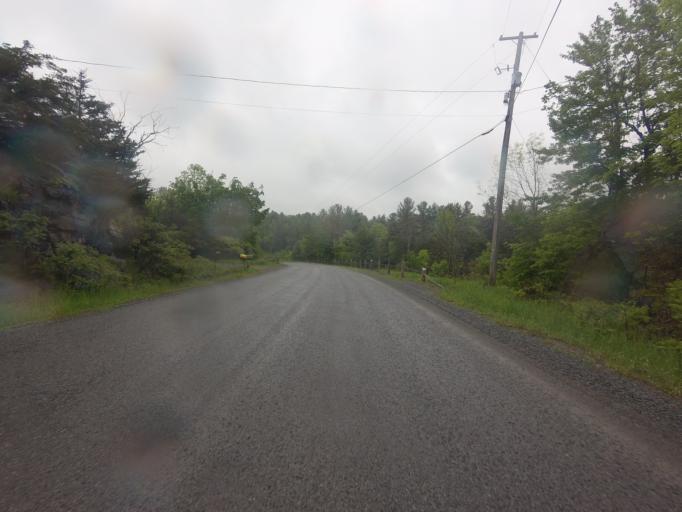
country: CA
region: Ontario
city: Kingston
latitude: 44.4819
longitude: -76.4682
